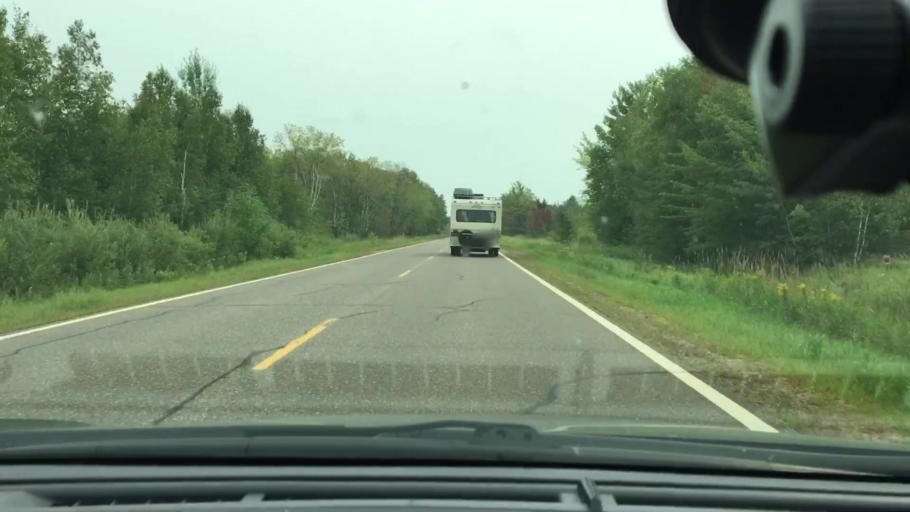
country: US
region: Minnesota
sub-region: Aitkin County
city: Aitkin
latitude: 46.4026
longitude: -93.7550
